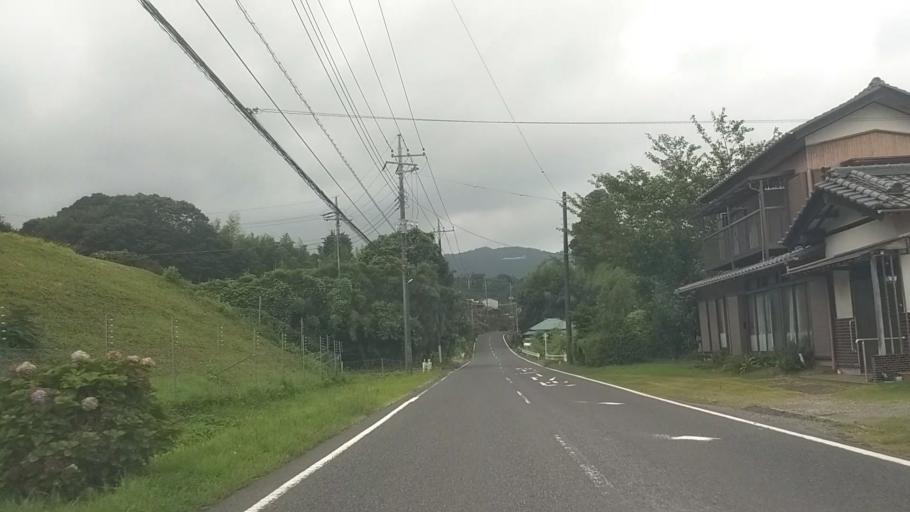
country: JP
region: Chiba
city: Kimitsu
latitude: 35.2442
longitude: 139.9952
